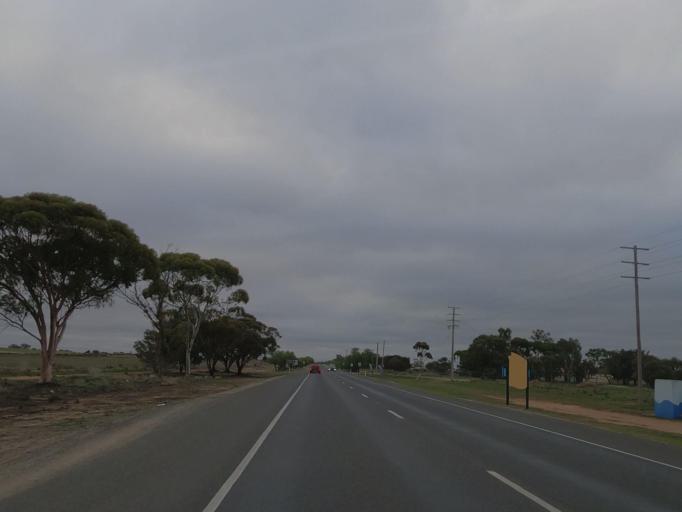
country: AU
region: Victoria
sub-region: Swan Hill
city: Swan Hill
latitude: -35.4510
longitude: 143.6246
